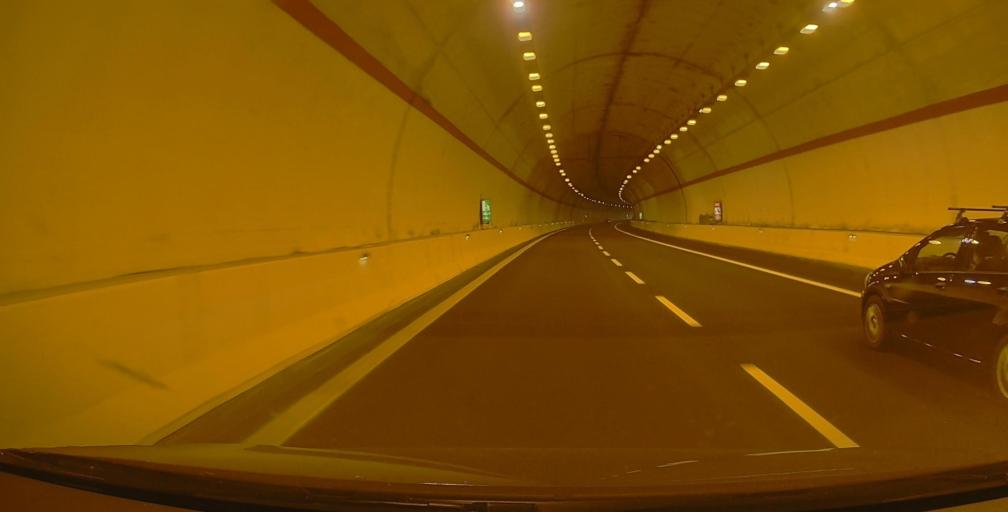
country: IT
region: Calabria
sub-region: Provincia di Vibo-Valentia
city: Filogaso
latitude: 38.6552
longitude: 16.1889
